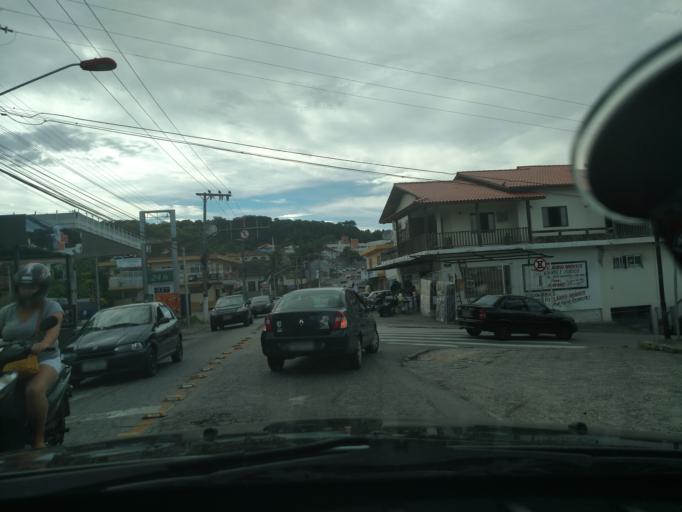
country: BR
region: Santa Catarina
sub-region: Sao Jose
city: Campinas
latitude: -27.6012
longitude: -48.6397
